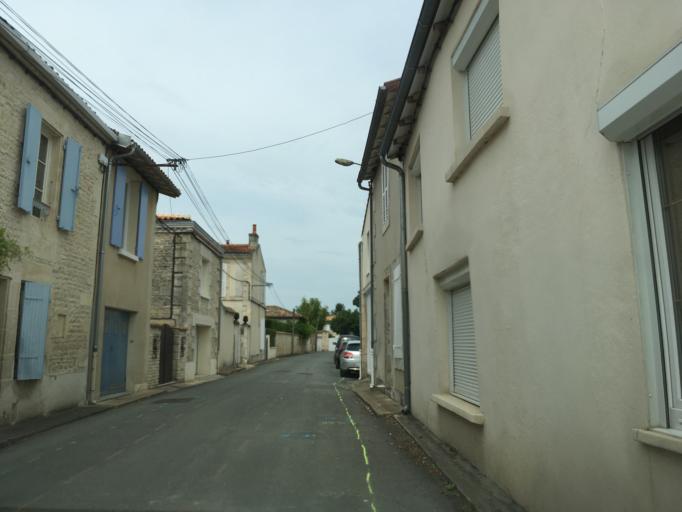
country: FR
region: Poitou-Charentes
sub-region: Departement des Deux-Sevres
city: Bessines
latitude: 46.3277
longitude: -0.5149
